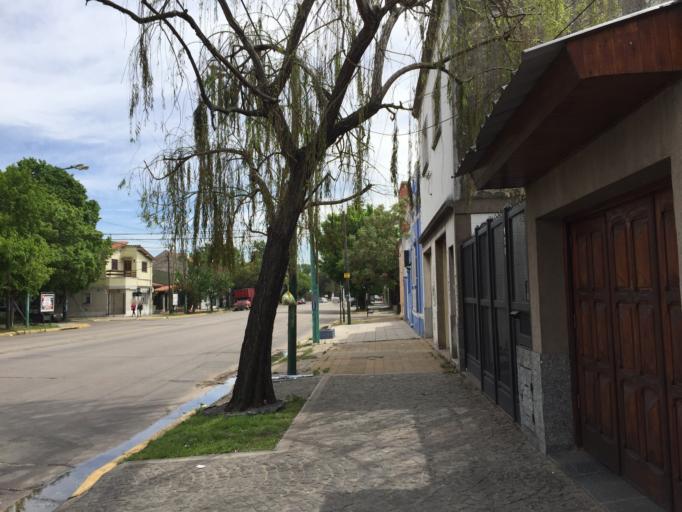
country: AR
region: Buenos Aires
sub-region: Partido de Lomas de Zamora
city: Lomas de Zamora
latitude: -34.7380
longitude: -58.3921
